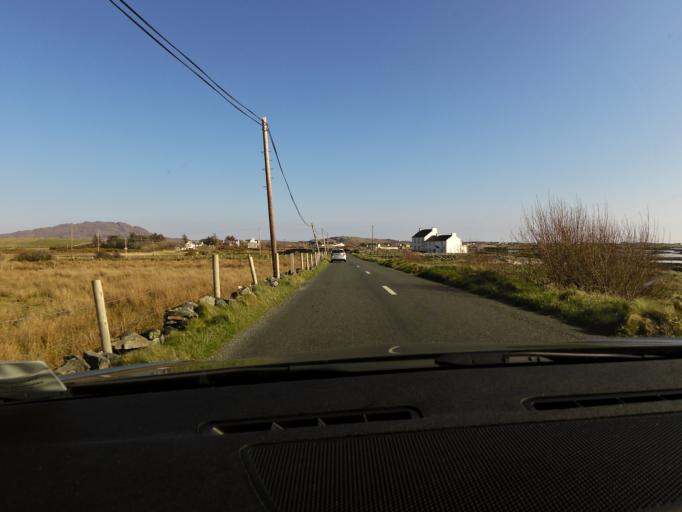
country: IE
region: Connaught
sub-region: County Galway
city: Clifden
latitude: 53.4110
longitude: -10.0391
